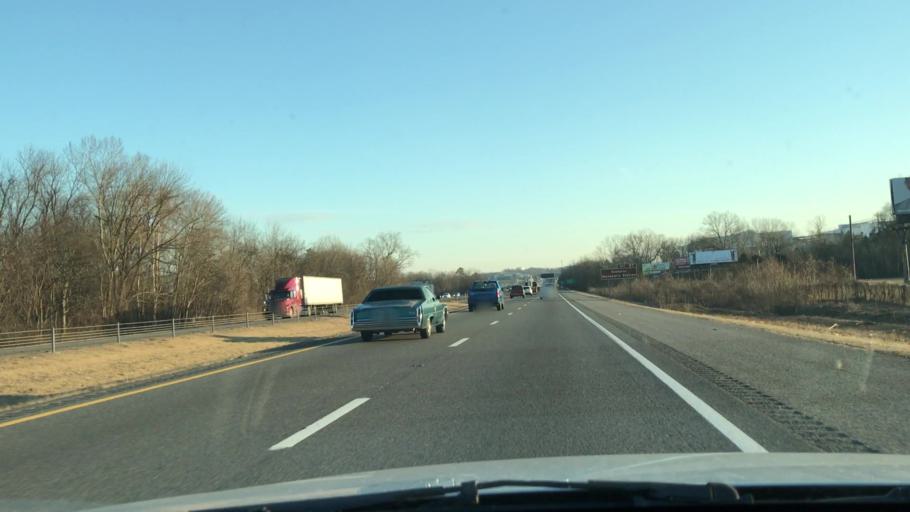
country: US
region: Tennessee
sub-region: Davidson County
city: Goodlettsville
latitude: 36.3376
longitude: -86.7119
